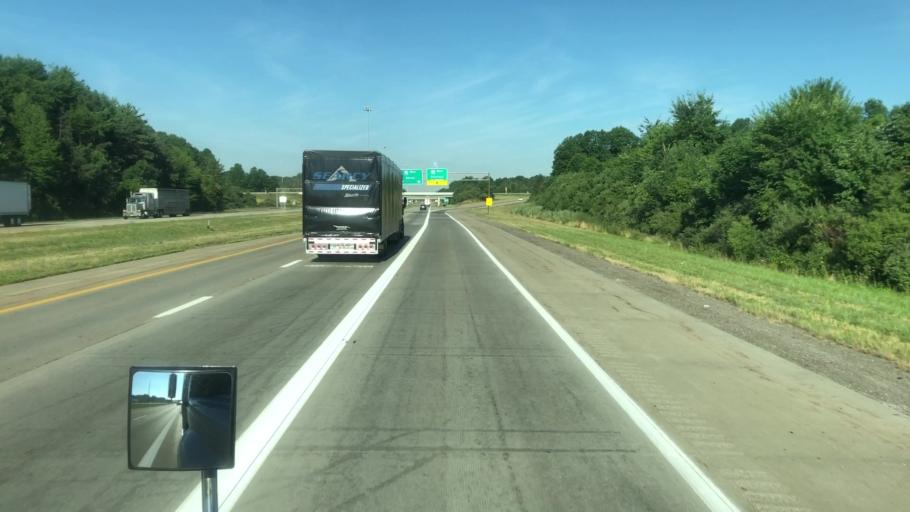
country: US
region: Ohio
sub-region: Trumbull County
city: Lordstown
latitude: 41.1111
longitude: -80.8268
